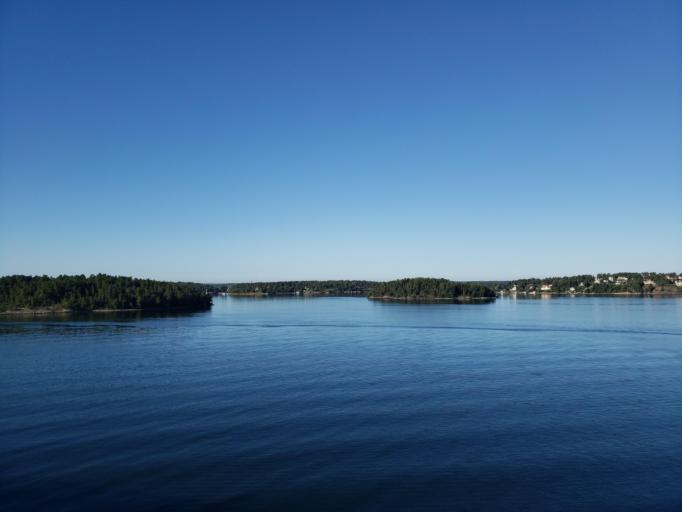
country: SE
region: Stockholm
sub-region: Vaxholms Kommun
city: Vaxholm
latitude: 59.4321
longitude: 18.3834
